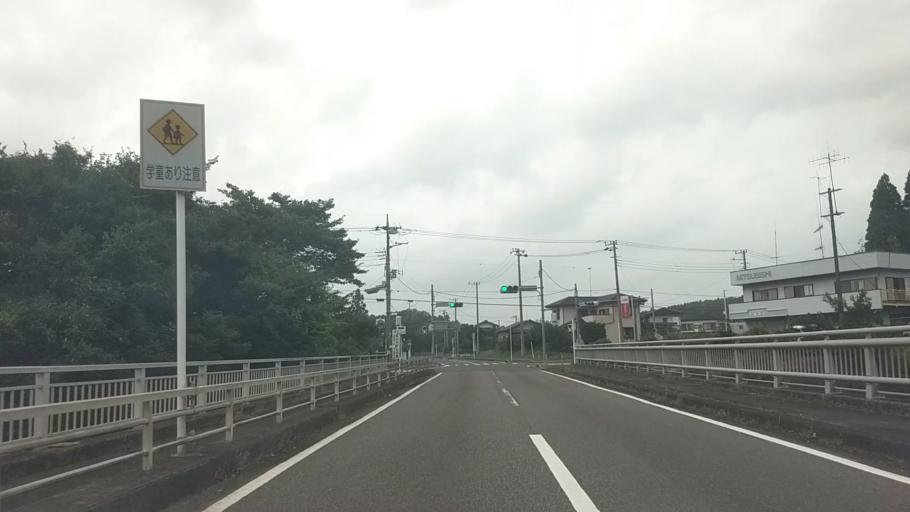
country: JP
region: Chiba
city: Kawaguchi
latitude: 35.2298
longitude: 140.0890
